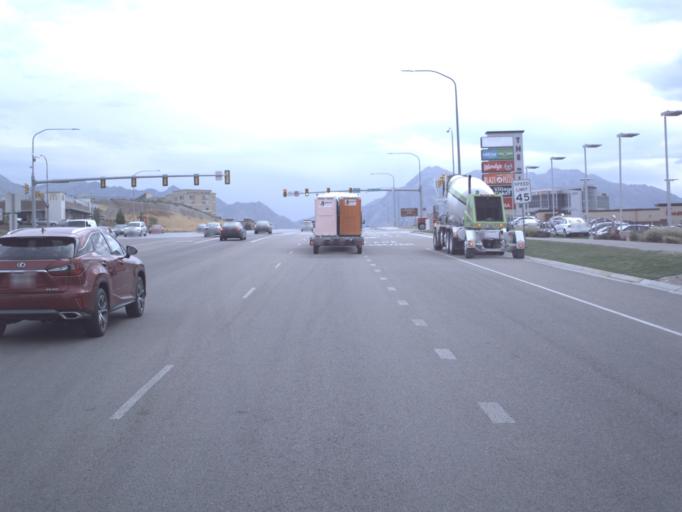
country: US
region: Utah
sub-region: Utah County
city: Lehi
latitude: 40.4314
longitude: -111.8883
